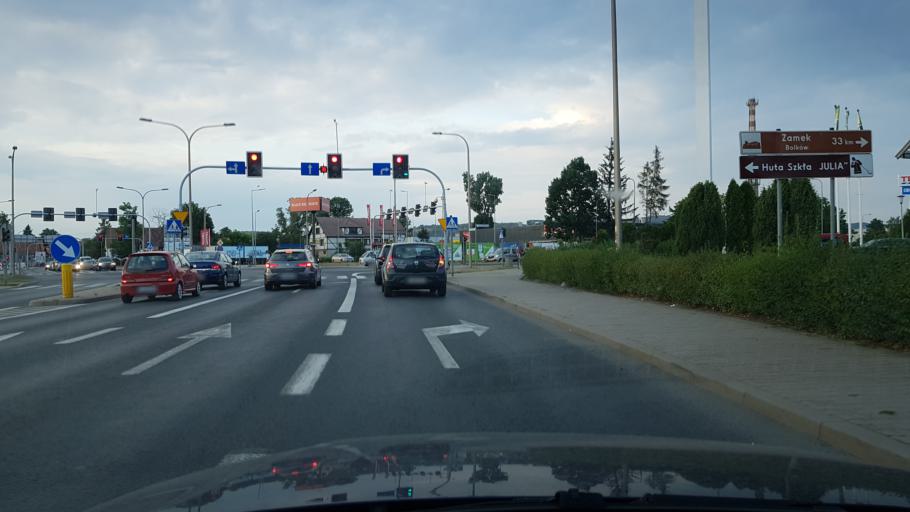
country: PL
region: Lower Silesian Voivodeship
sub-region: Jelenia Gora
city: Jelenia Gora
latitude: 50.9079
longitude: 15.7362
